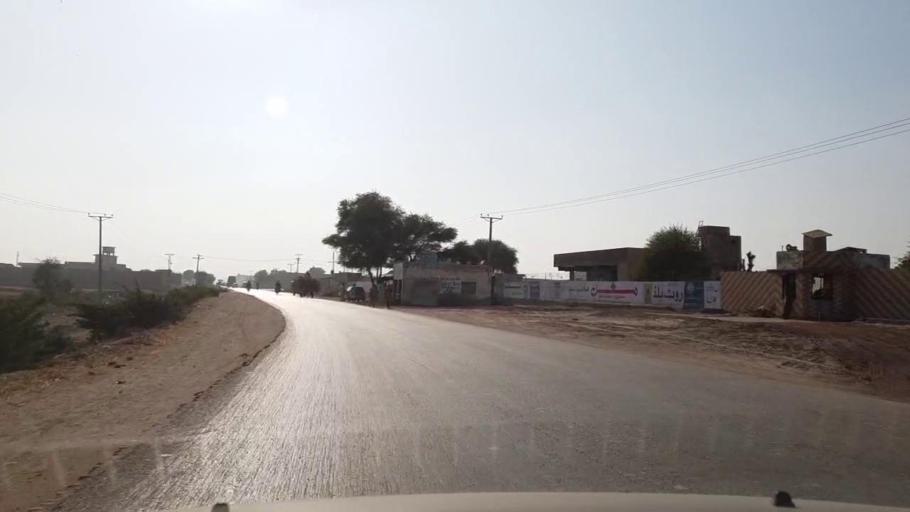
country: PK
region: Sindh
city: Tando Muhammad Khan
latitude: 25.1122
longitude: 68.5241
